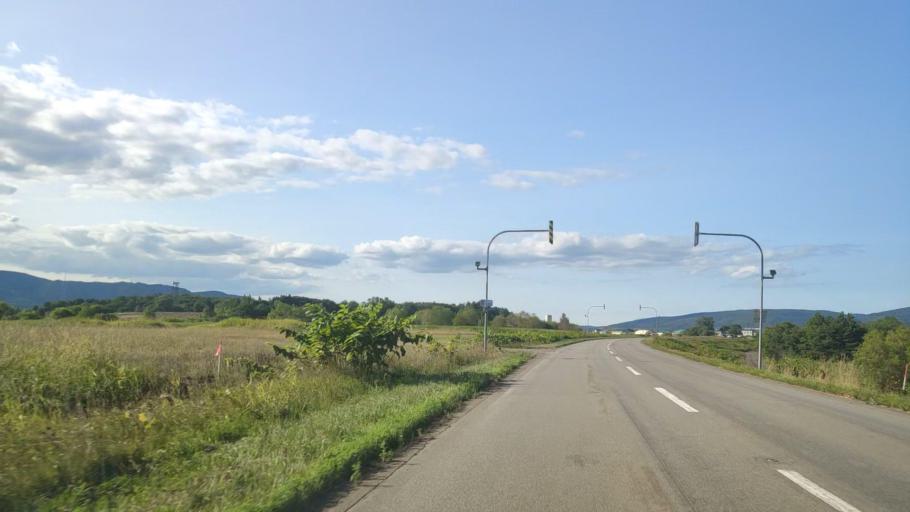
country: JP
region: Hokkaido
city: Nayoro
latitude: 44.8105
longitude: 142.0660
